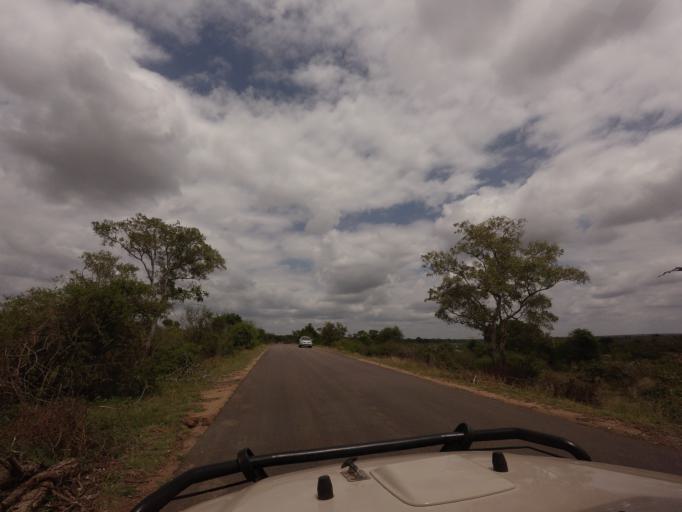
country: ZA
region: Mpumalanga
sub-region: Ehlanzeni District
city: Komatipoort
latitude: -25.1012
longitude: 31.8869
